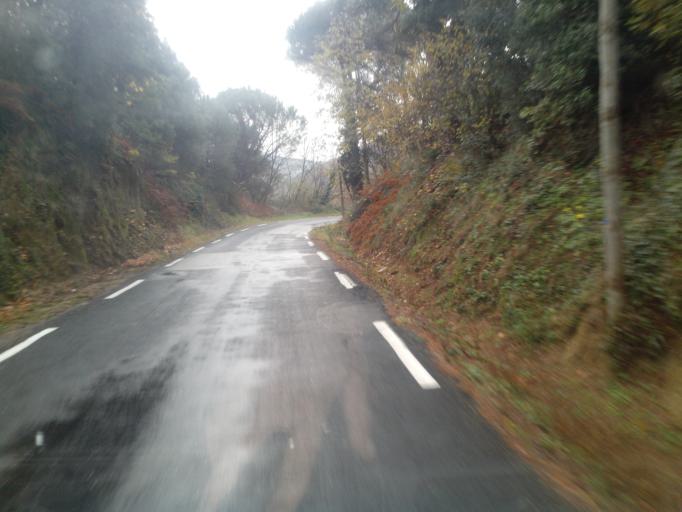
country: FR
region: Languedoc-Roussillon
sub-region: Departement du Gard
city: Lasalle
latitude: 44.0146
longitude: 3.8482
